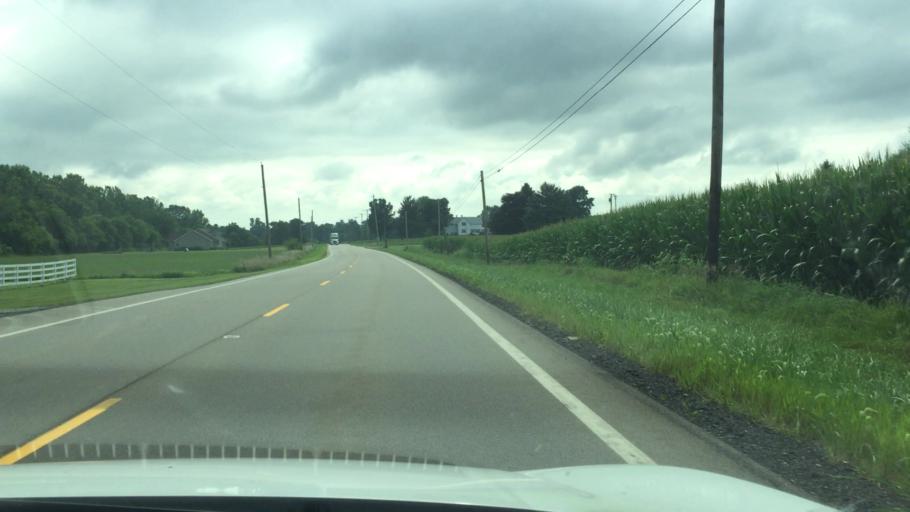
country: US
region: Ohio
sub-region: Champaign County
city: Mechanicsburg
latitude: 40.0606
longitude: -83.5870
